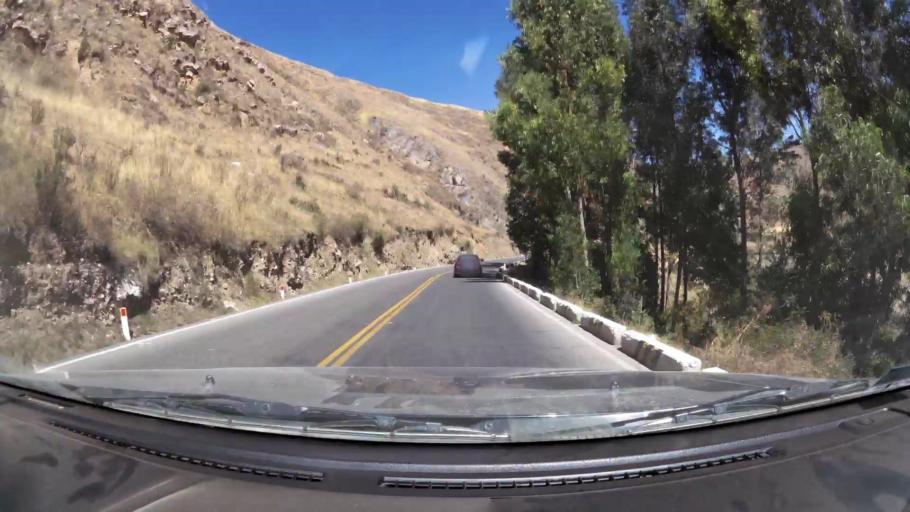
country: PE
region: Junin
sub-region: Provincia de Jauja
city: Huaripampa
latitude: -11.8139
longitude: -75.4921
